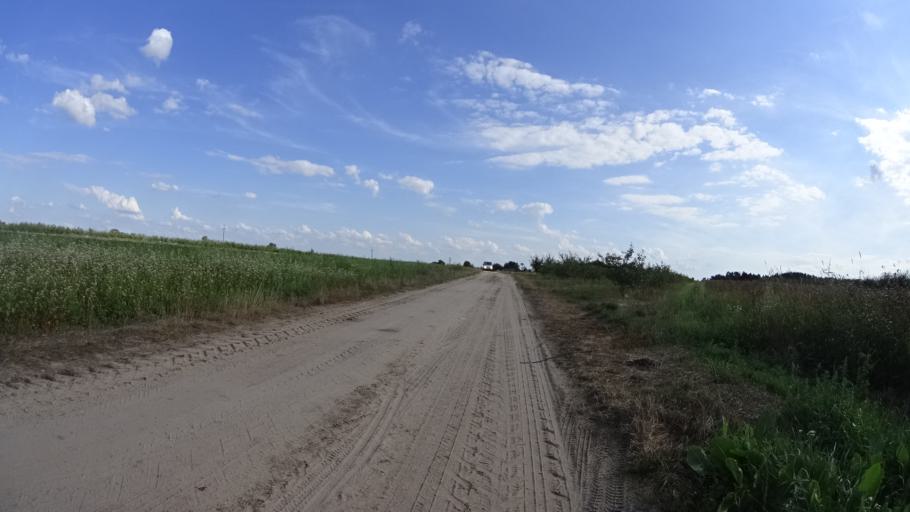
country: PL
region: Masovian Voivodeship
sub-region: Powiat bialobrzeski
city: Wysmierzyce
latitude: 51.6601
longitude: 20.8204
